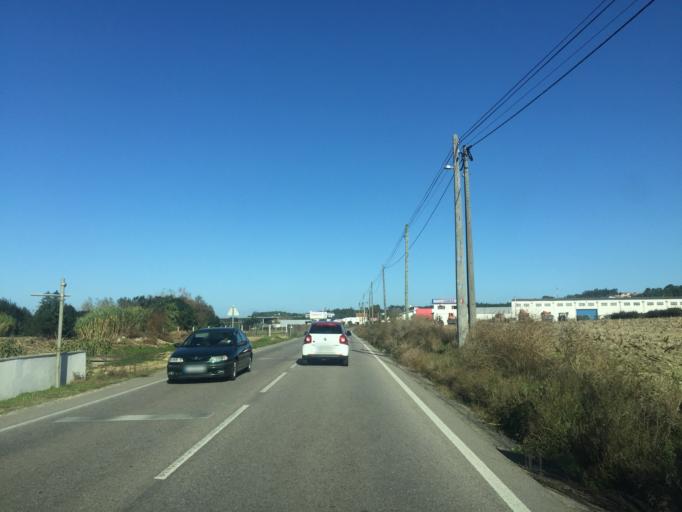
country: PT
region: Leiria
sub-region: Leiria
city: Amor
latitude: 39.7975
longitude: -8.8367
